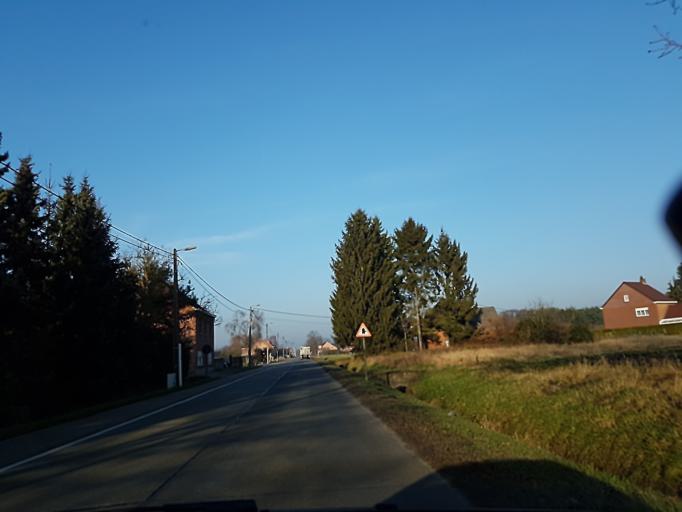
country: BE
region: Flanders
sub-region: Provincie Vlaams-Brabant
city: Tremelo
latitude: 51.0234
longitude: 4.7106
